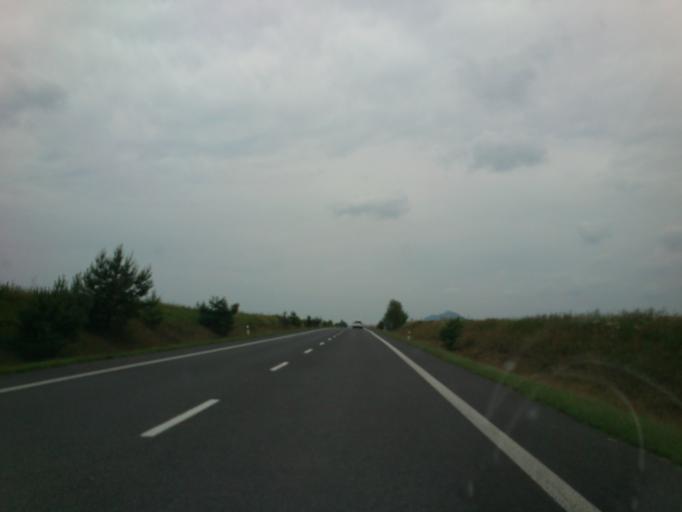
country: CZ
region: Central Bohemia
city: Bela pod Bezdezem
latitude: 50.4873
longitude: 14.8196
